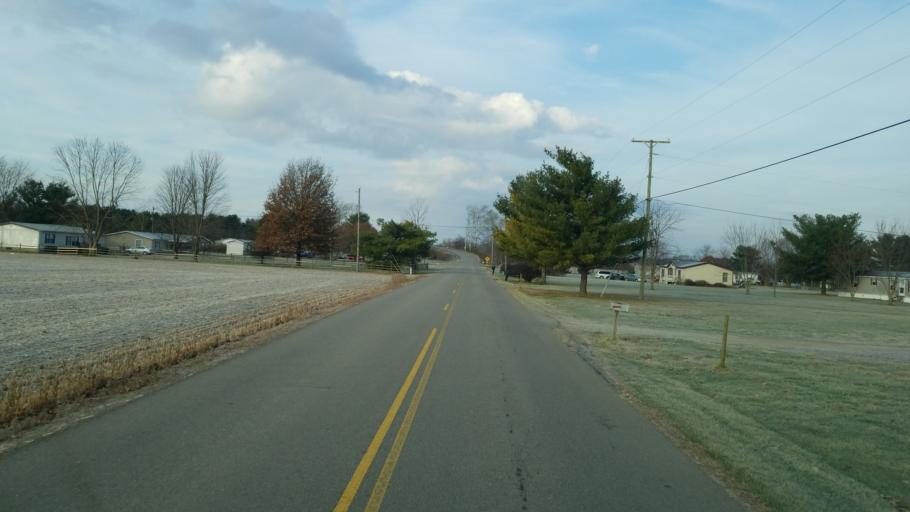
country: US
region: Ohio
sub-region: Ross County
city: Chillicothe
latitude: 39.2520
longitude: -82.8661
